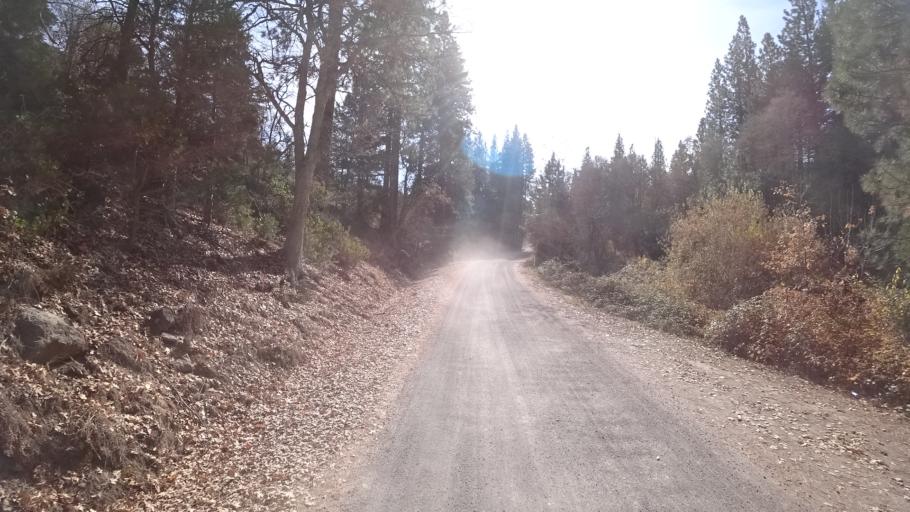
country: US
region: California
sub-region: Siskiyou County
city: Weed
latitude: 41.4391
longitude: -122.4241
